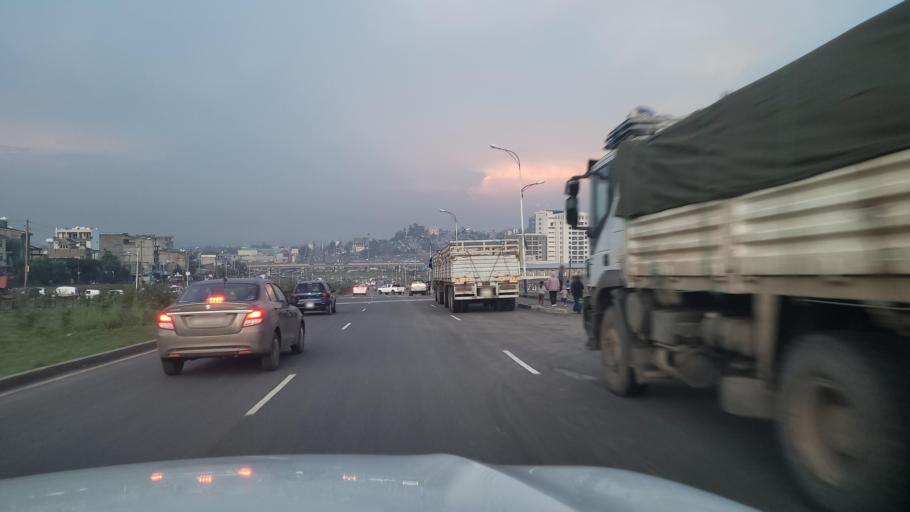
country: ET
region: Adis Abeba
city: Addis Ababa
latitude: 8.9382
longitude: 38.7296
